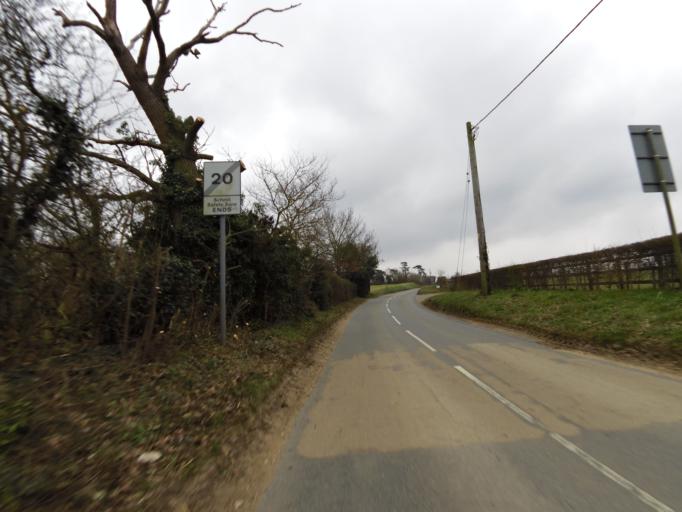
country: GB
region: England
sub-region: Suffolk
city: Wickham Market
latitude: 52.1760
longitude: 1.3432
